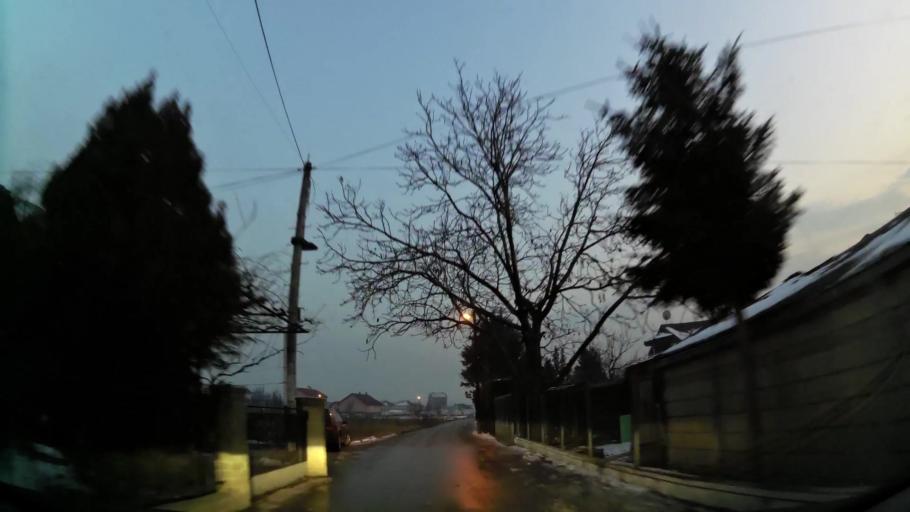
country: MK
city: Creshevo
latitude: 42.0068
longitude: 21.5125
